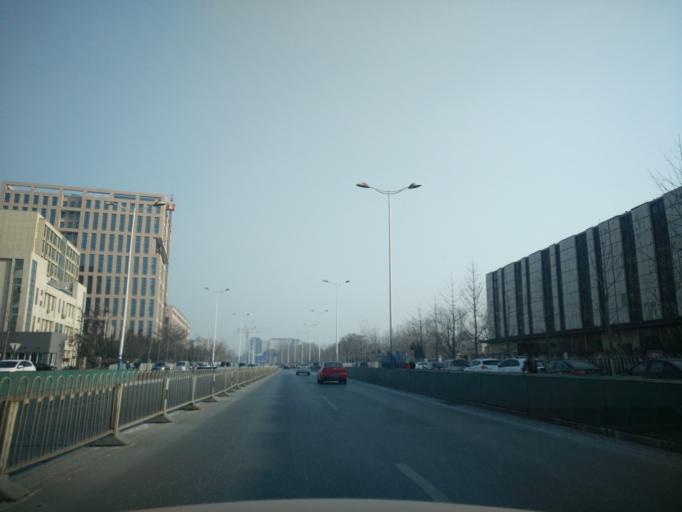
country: CN
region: Beijing
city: Daxing
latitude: 39.7418
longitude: 116.3198
